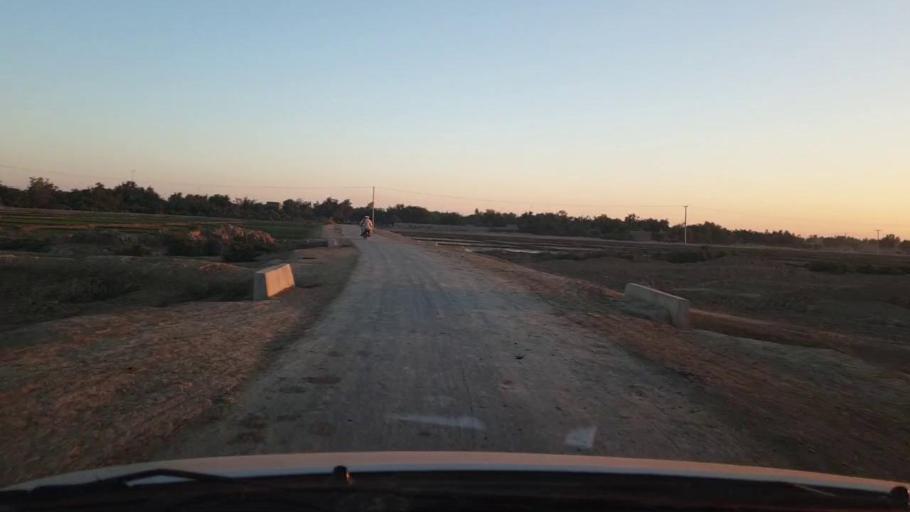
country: PK
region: Sindh
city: Johi
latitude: 26.8336
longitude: 67.4422
